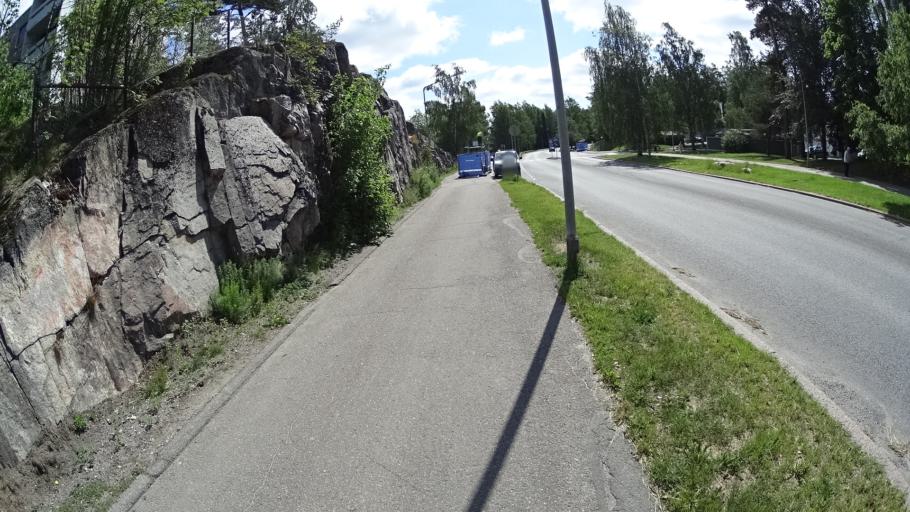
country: FI
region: Uusimaa
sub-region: Helsinki
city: Vantaa
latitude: 60.2362
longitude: 25.1260
